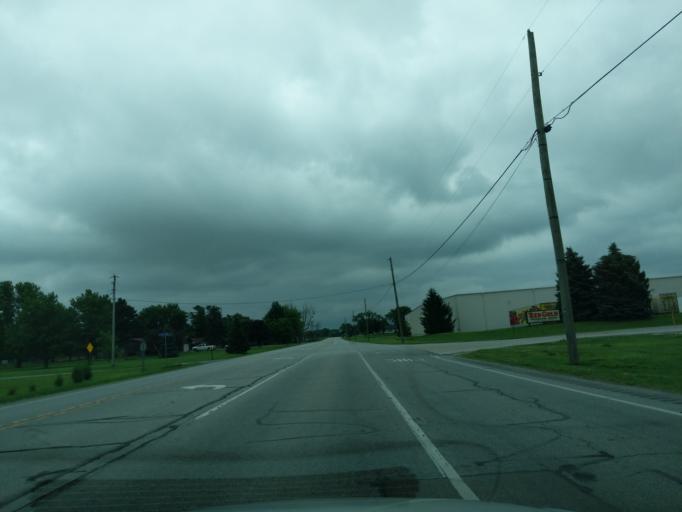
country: US
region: Indiana
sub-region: Madison County
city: Alexandria
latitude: 40.2774
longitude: -85.7224
